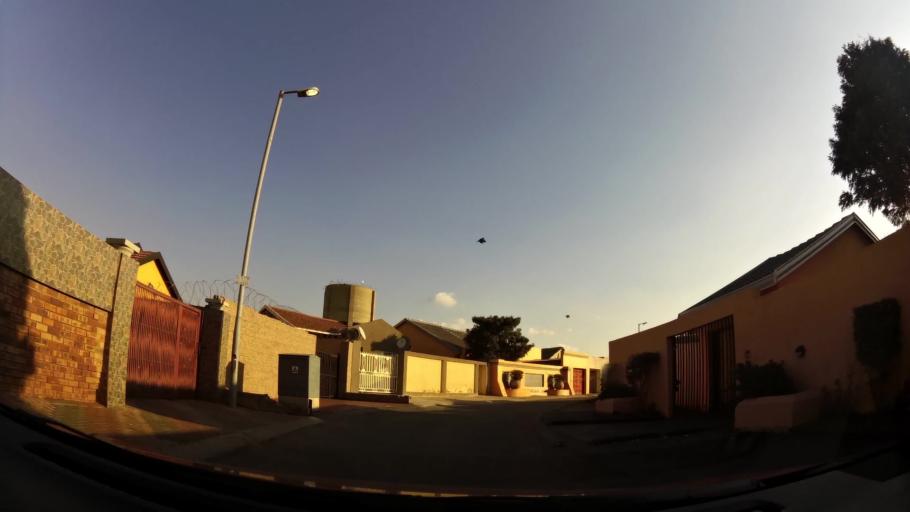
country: ZA
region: Gauteng
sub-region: City of Johannesburg Metropolitan Municipality
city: Soweto
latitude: -26.2306
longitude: 27.8558
